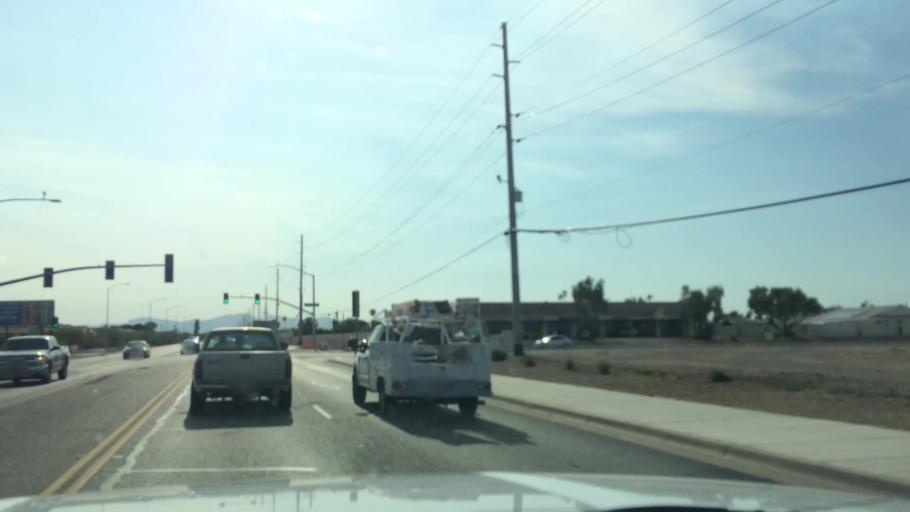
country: US
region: Arizona
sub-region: Maricopa County
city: Sun City
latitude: 33.5658
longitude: -112.2753
